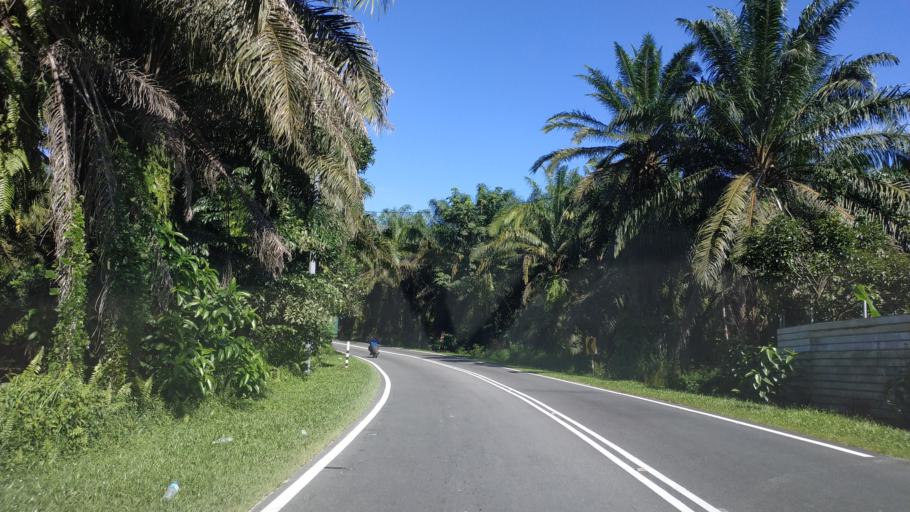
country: MY
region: Kedah
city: Kulim
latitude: 5.3220
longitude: 100.5373
